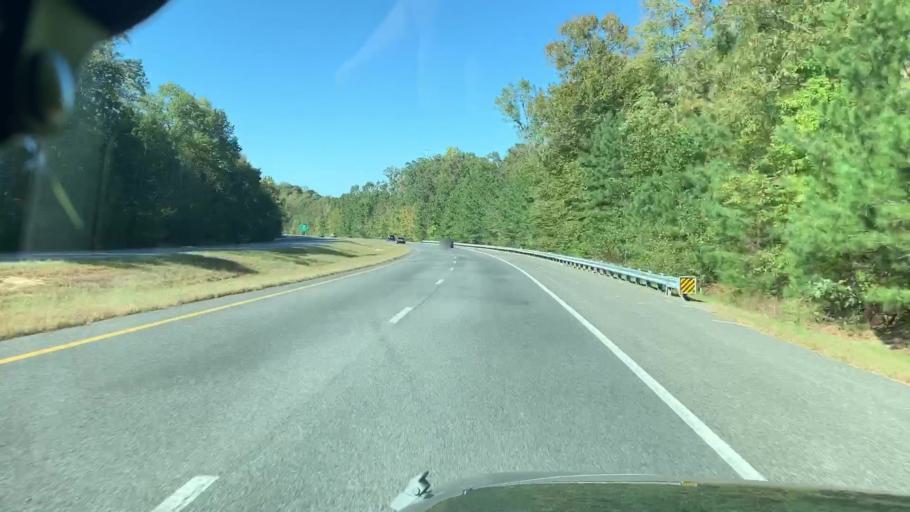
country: US
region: Virginia
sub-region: James City County
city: Williamsburg
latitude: 37.3173
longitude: -76.7494
